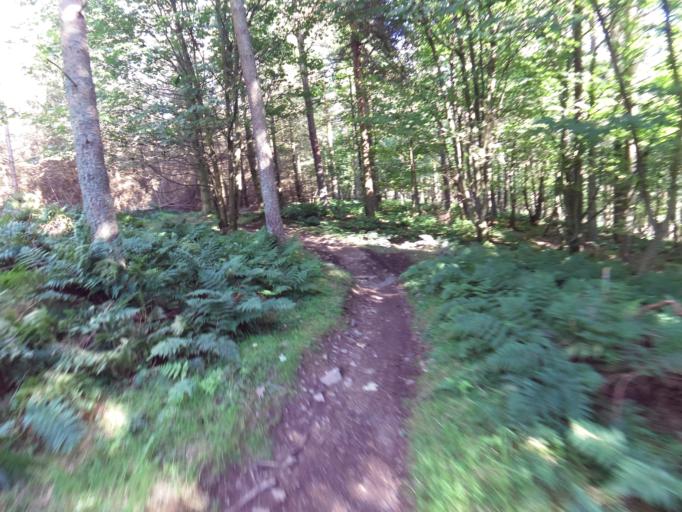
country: GB
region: Scotland
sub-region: The Scottish Borders
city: Peebles
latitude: 55.6515
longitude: -3.1385
